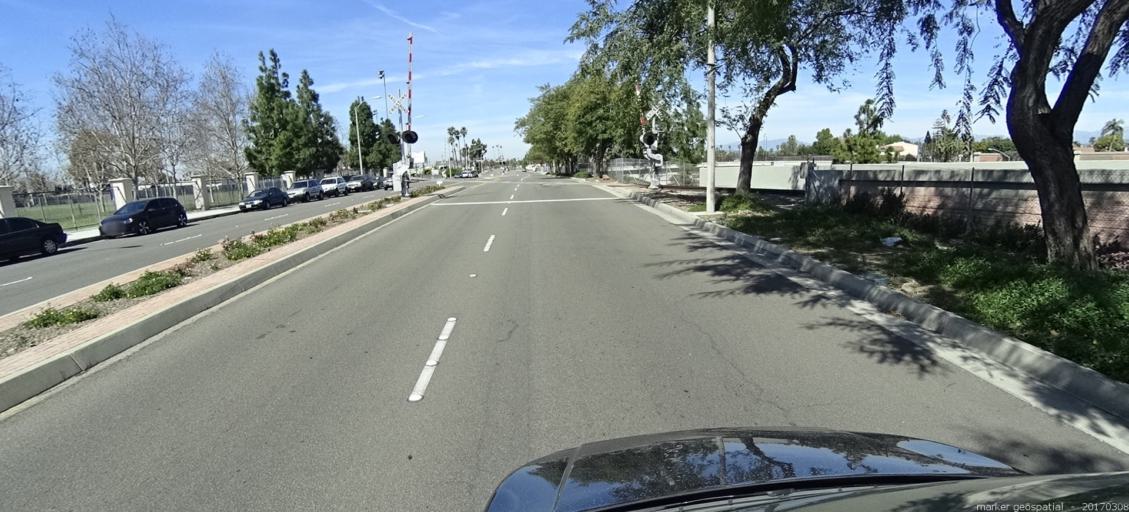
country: US
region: California
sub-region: Orange County
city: Anaheim
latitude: 33.8280
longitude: -117.9284
